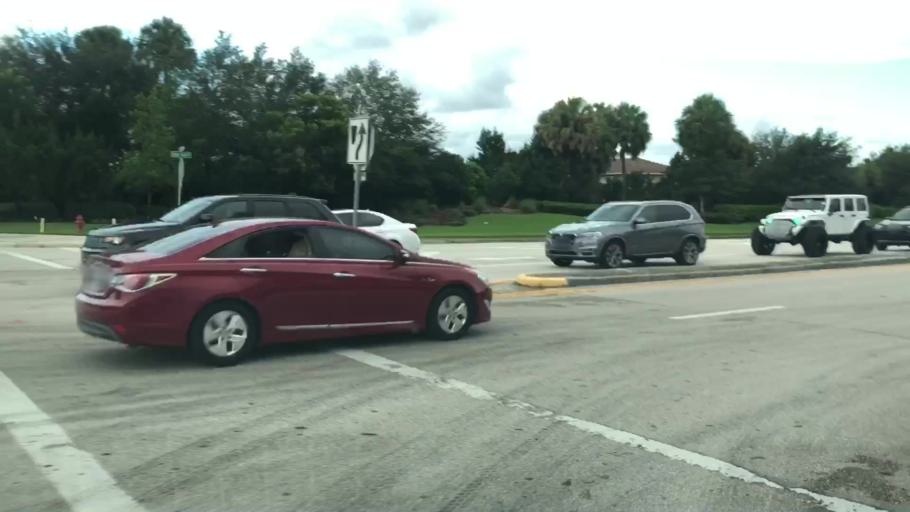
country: US
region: Florida
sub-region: Broward County
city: Parkland
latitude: 26.3342
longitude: -80.2673
